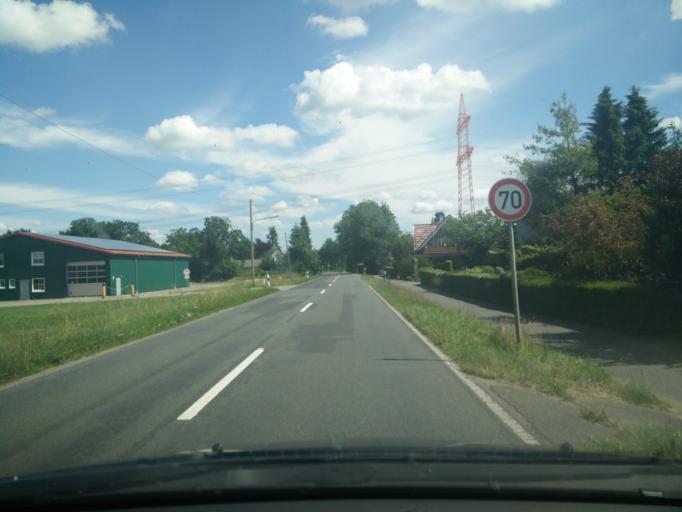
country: DE
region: Schleswig-Holstein
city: Prisdorf
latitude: 53.6826
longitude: 9.7348
